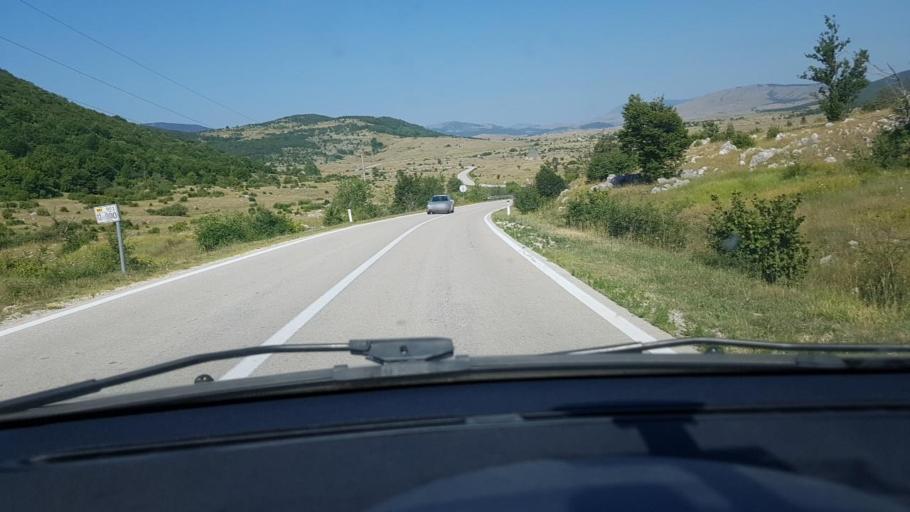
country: BA
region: Federation of Bosnia and Herzegovina
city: Bosansko Grahovo
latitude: 44.1298
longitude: 16.4940
